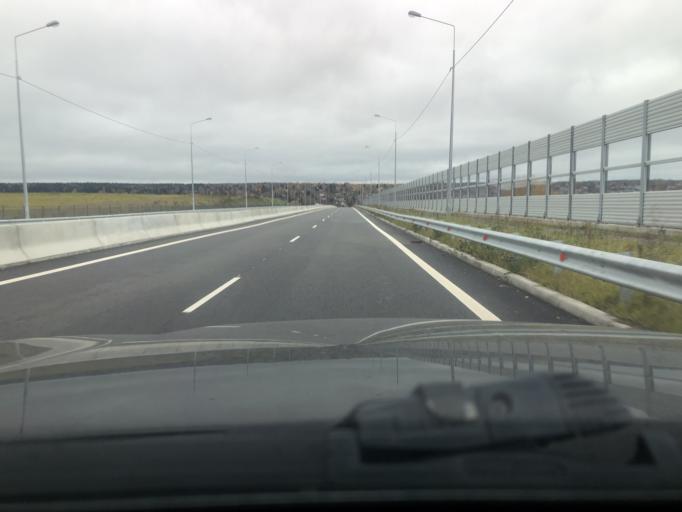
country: RU
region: Moskovskaya
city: Sergiyev Posad
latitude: 56.2939
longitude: 38.1043
